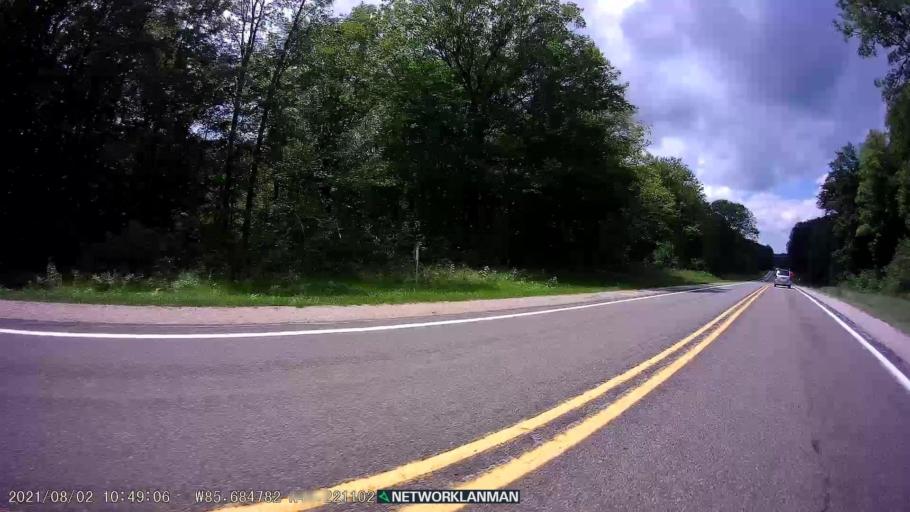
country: US
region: Michigan
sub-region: Wexford County
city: Cadillac
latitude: 44.2214
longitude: -85.6850
